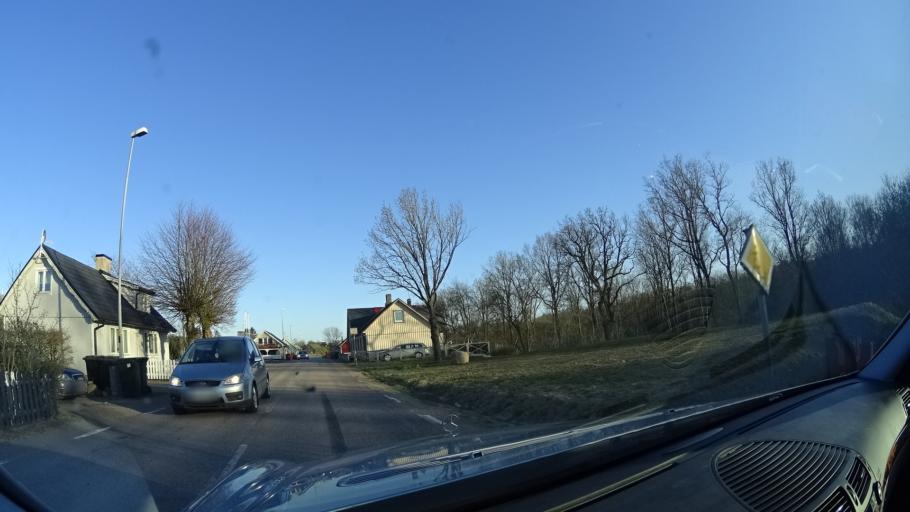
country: SE
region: Skane
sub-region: Bjuvs Kommun
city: Billesholm
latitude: 56.0560
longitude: 12.9949
